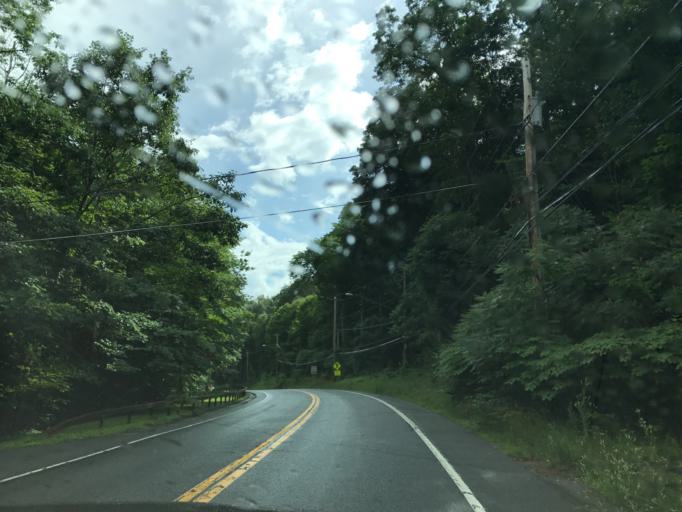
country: US
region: New York
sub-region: Warren County
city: Warrensburg
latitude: 43.5469
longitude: -73.6641
